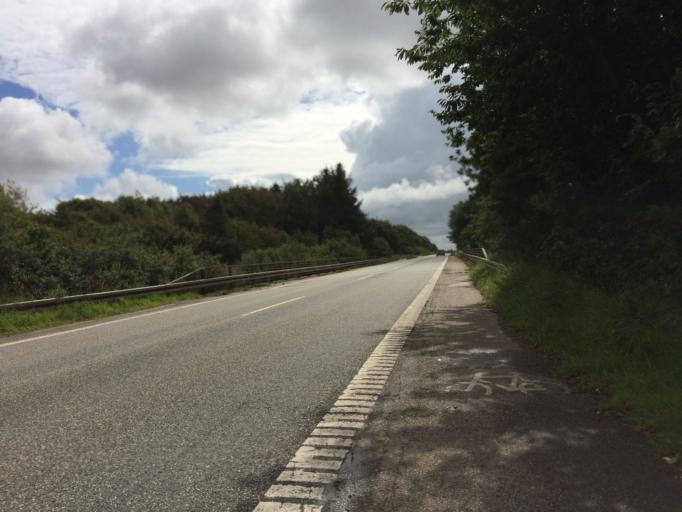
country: DK
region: Central Jutland
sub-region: Holstebro Kommune
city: Ulfborg
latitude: 56.3355
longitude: 8.3453
